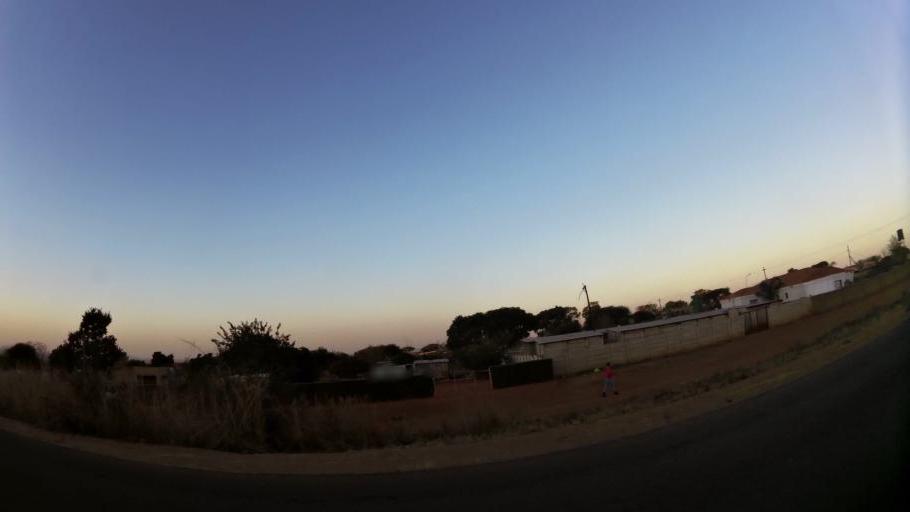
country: ZA
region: North-West
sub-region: Bojanala Platinum District Municipality
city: Rustenburg
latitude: -25.6241
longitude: 27.1971
